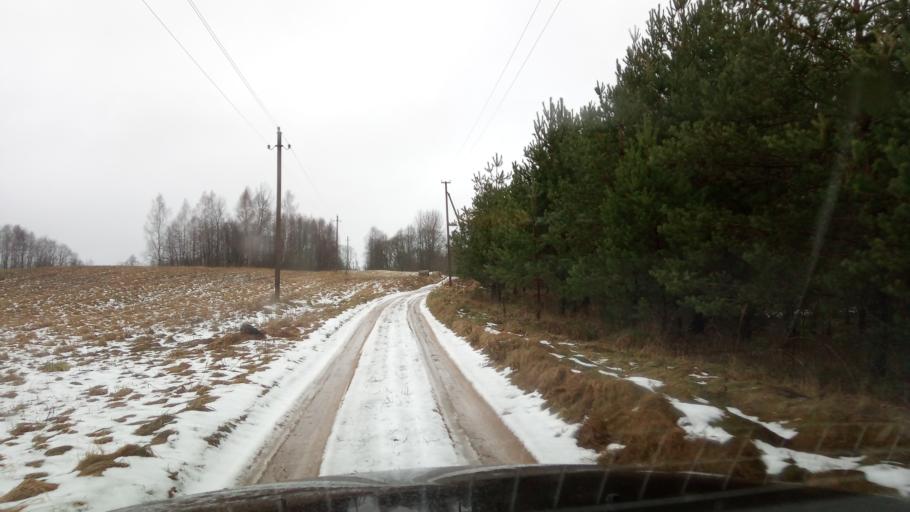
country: LT
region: Utenos apskritis
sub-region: Utena
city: Utena
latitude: 55.3694
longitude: 25.7636
